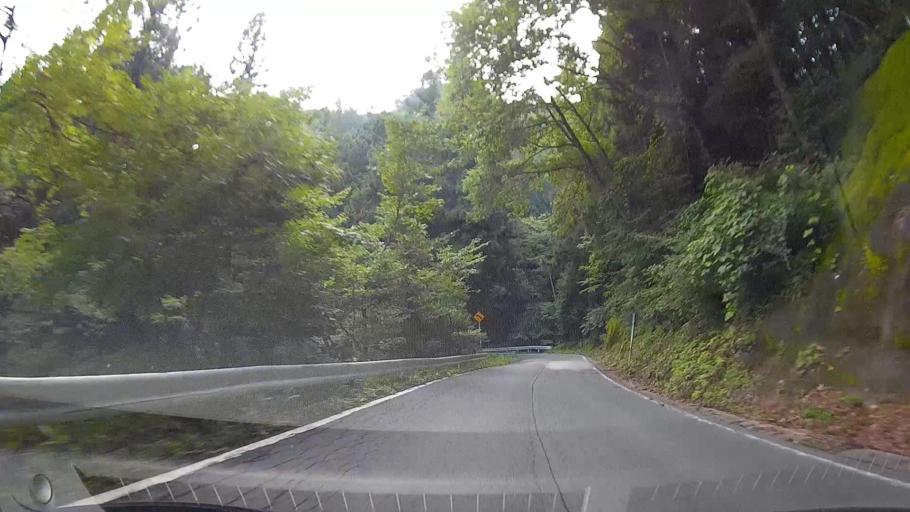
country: JP
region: Gunma
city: Nakanojomachi
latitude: 36.6173
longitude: 138.6362
